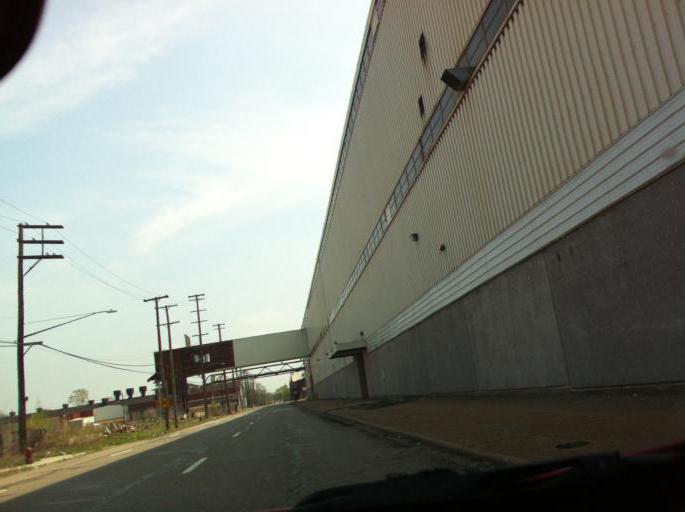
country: US
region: Michigan
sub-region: Wayne County
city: River Rouge
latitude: 42.3055
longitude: -83.1028
